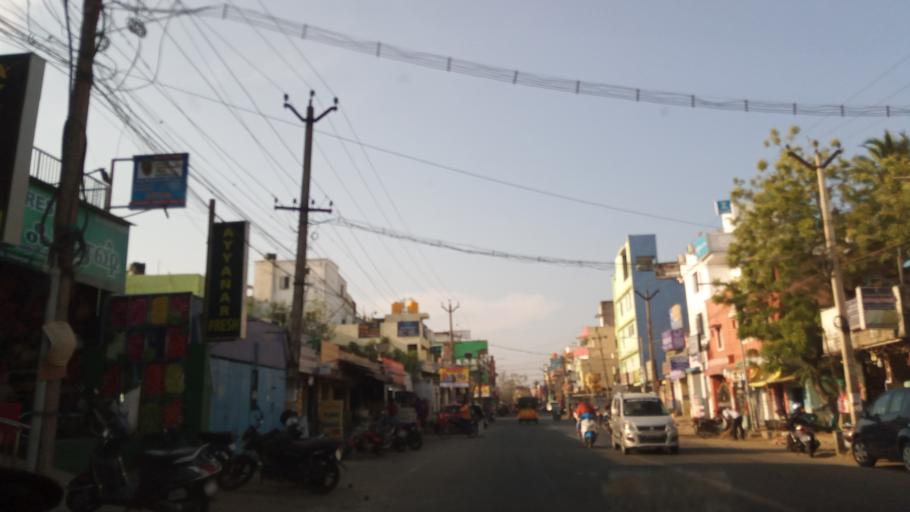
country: IN
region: Tamil Nadu
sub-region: Kancheepuram
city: Manappakkam
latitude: 13.0290
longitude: 80.1835
